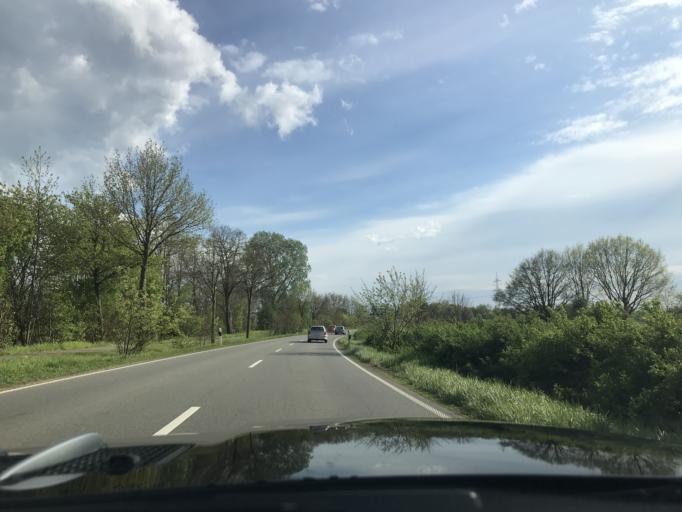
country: DE
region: Schleswig-Holstein
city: Hornbek
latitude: 53.5563
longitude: 10.6491
